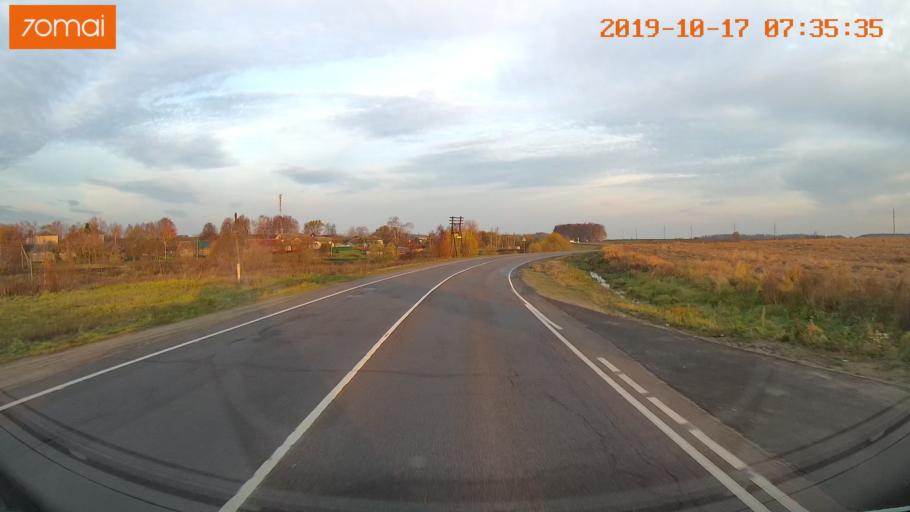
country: RU
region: Ivanovo
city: Gavrilov Posad
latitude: 56.4295
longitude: 39.9259
